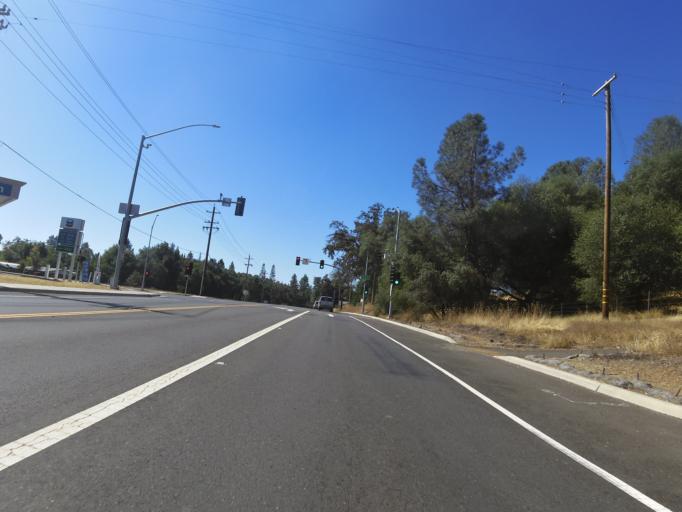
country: US
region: California
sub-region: El Dorado County
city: Deer Park
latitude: 38.6893
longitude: -120.8313
